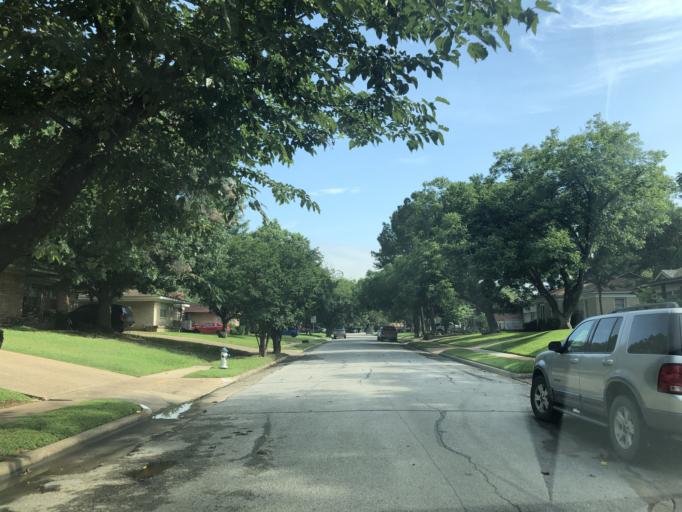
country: US
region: Texas
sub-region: Dallas County
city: Irving
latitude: 32.7987
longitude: -96.9609
